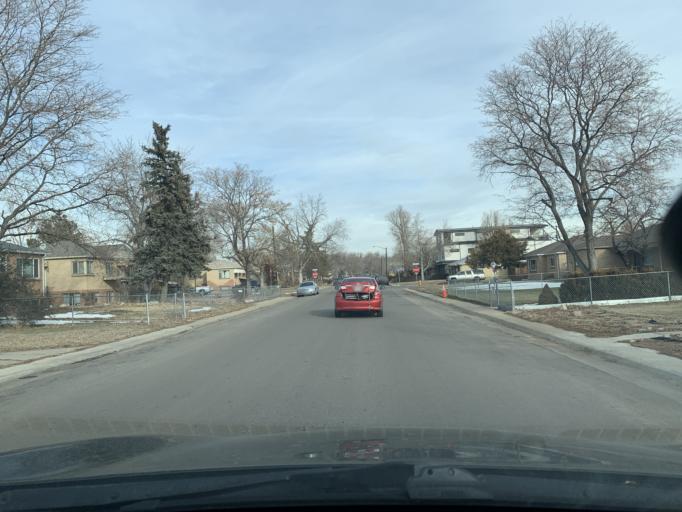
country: US
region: Colorado
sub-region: Jefferson County
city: Edgewater
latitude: 39.7488
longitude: -105.0544
